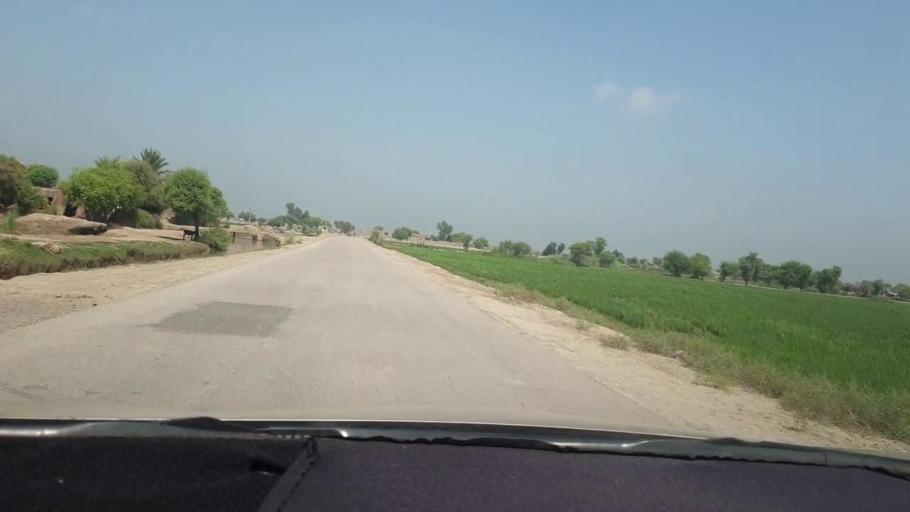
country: PK
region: Sindh
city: Miro Khan
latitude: 27.7831
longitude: 68.0526
